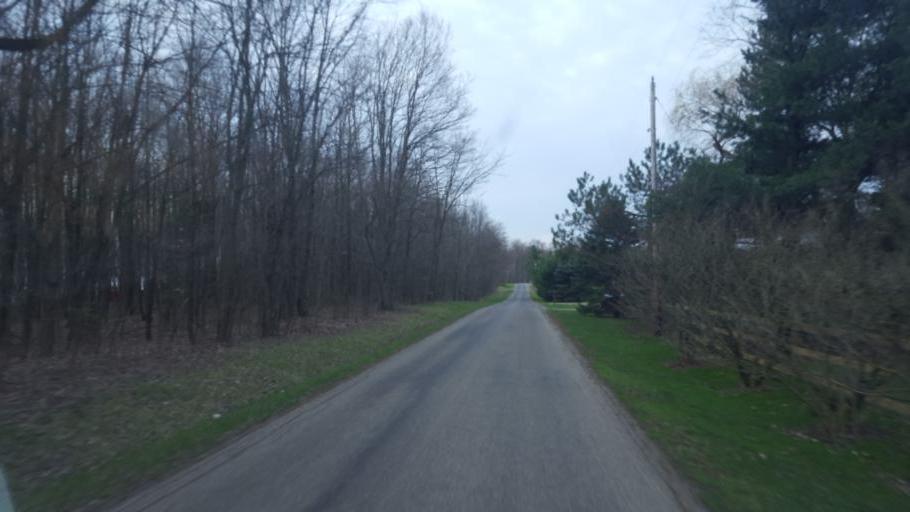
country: US
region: Ohio
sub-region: Sandusky County
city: Bellville
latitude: 40.5705
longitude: -82.5801
